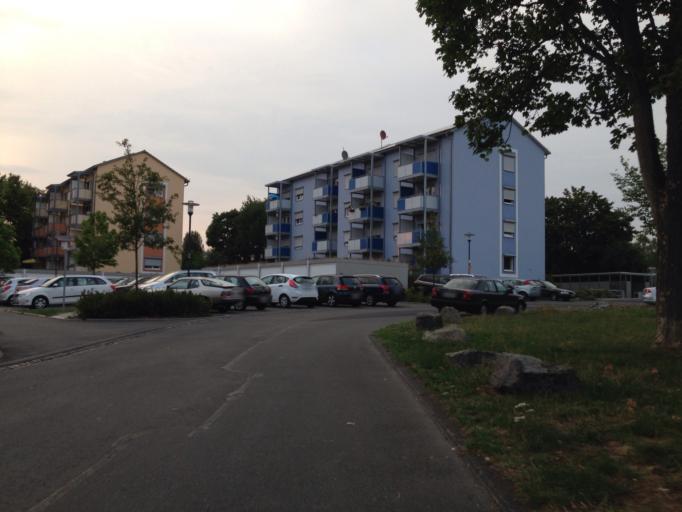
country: DE
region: Hesse
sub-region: Regierungsbezirk Giessen
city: Giessen
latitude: 50.5988
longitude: 8.6821
